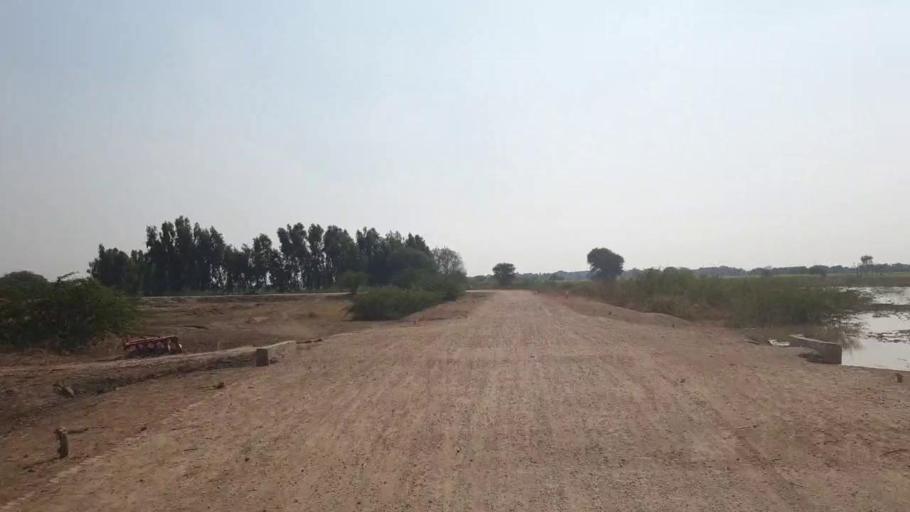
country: PK
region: Sindh
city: Chambar
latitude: 25.3530
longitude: 68.8987
